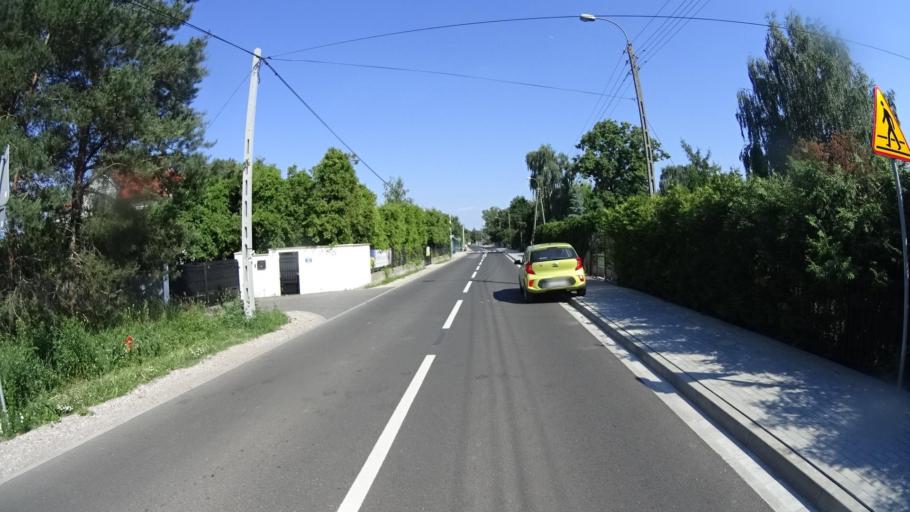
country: PL
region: Masovian Voivodeship
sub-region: Powiat warszawski zachodni
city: Blonie
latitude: 52.1669
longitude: 20.6246
